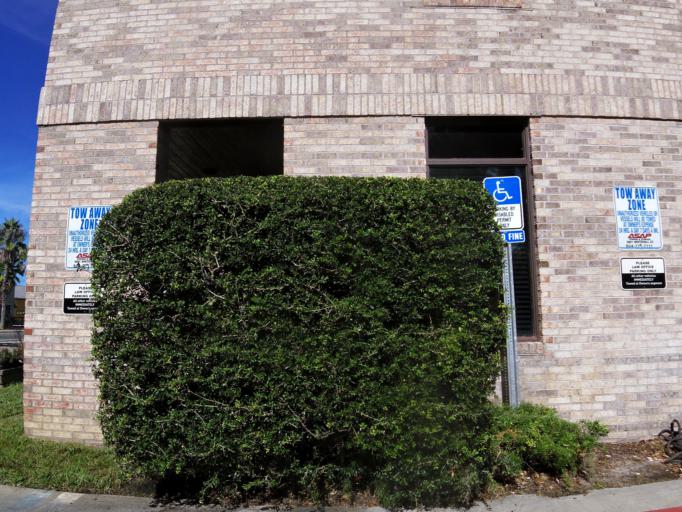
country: US
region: Florida
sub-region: Duval County
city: Jacksonville
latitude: 30.3066
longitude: -81.6536
